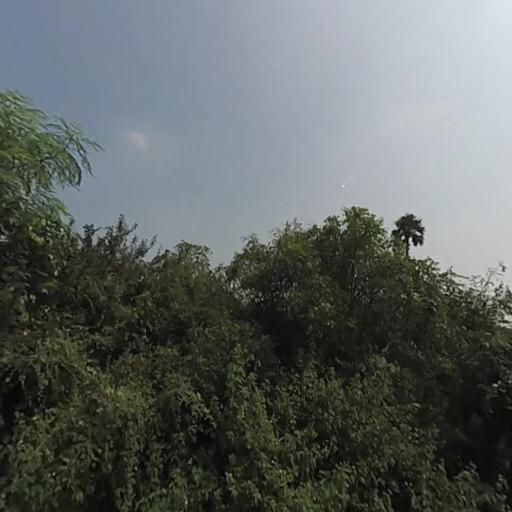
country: IN
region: Telangana
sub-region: Nalgonda
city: Nalgonda
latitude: 17.2065
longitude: 79.1542
